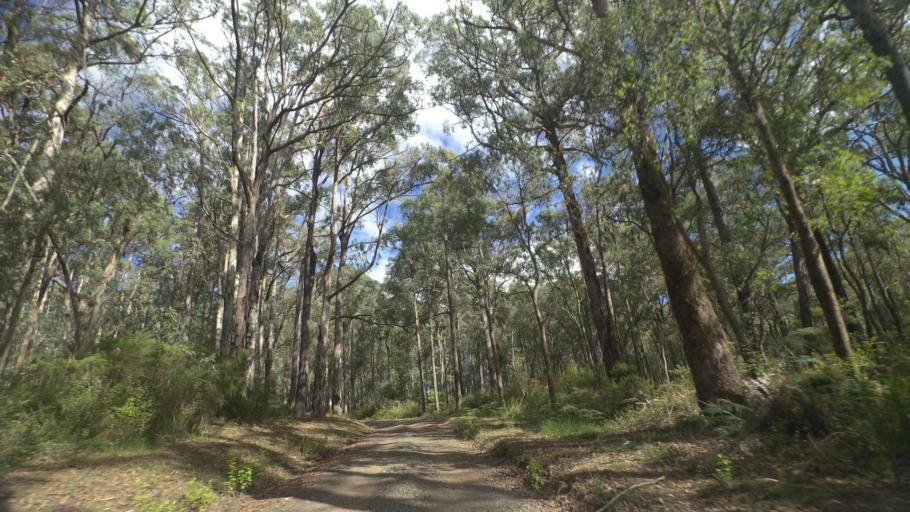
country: AU
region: Victoria
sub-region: Cardinia
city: Gembrook
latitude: -37.9115
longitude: 145.5995
